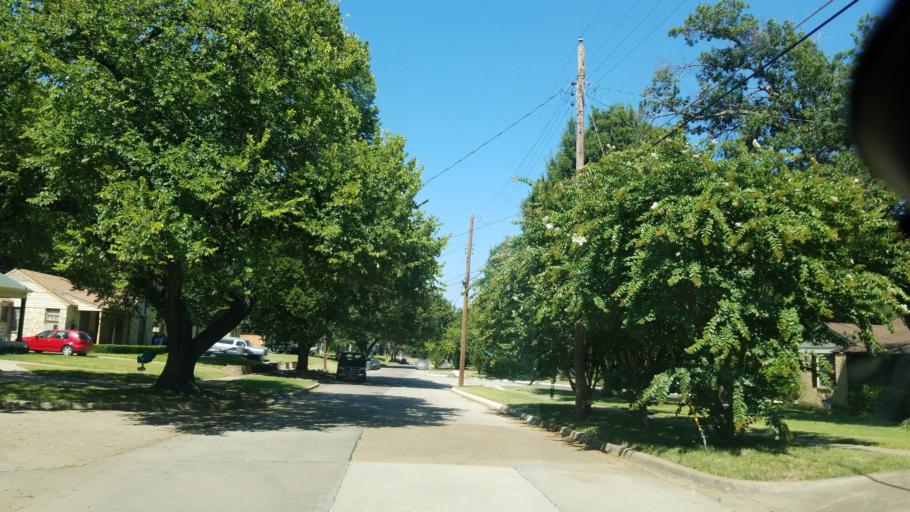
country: US
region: Texas
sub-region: Dallas County
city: Cockrell Hill
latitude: 32.7300
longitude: -96.8466
